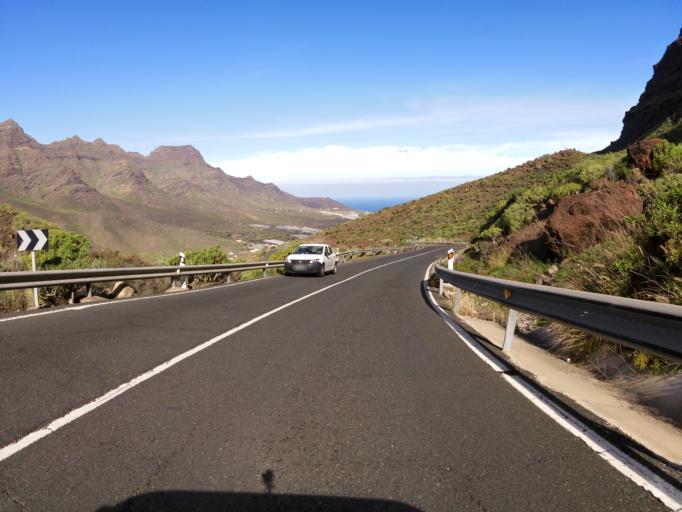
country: ES
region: Canary Islands
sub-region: Provincia de Las Palmas
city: San Nicolas
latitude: 27.9486
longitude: -15.7634
